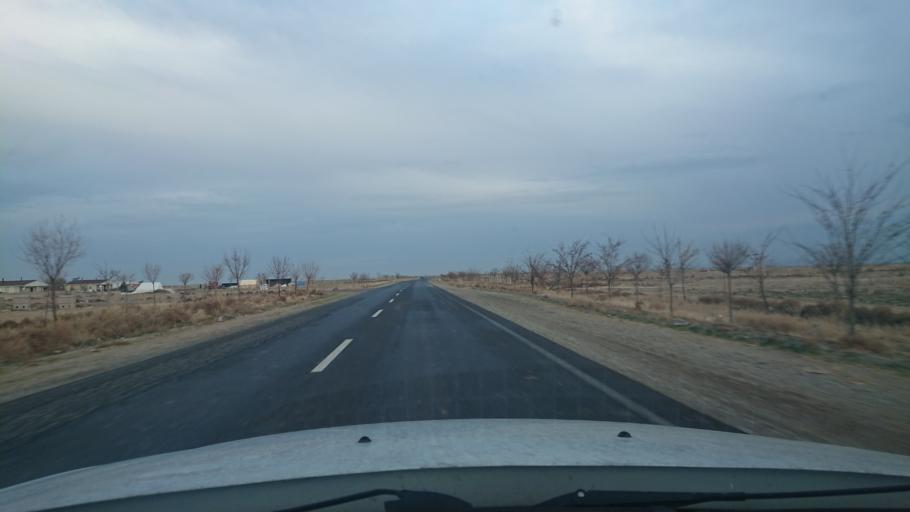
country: TR
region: Aksaray
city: Yesilova
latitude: 38.3060
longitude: 33.7551
